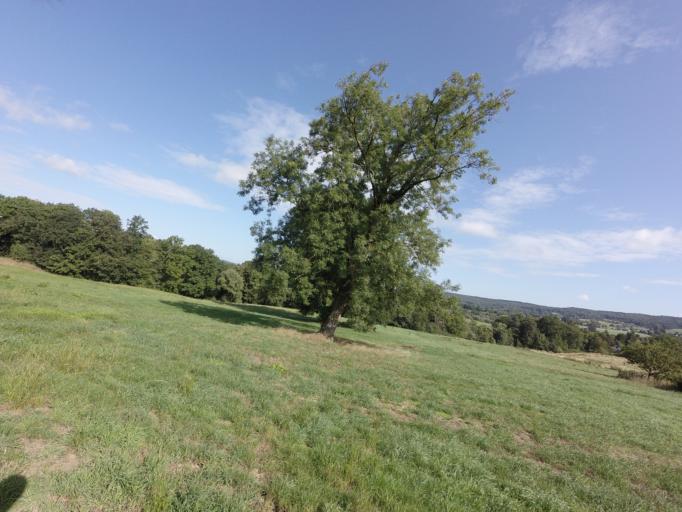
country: BE
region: Wallonia
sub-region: Province de Liege
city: Plombieres
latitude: 50.7425
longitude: 5.9444
